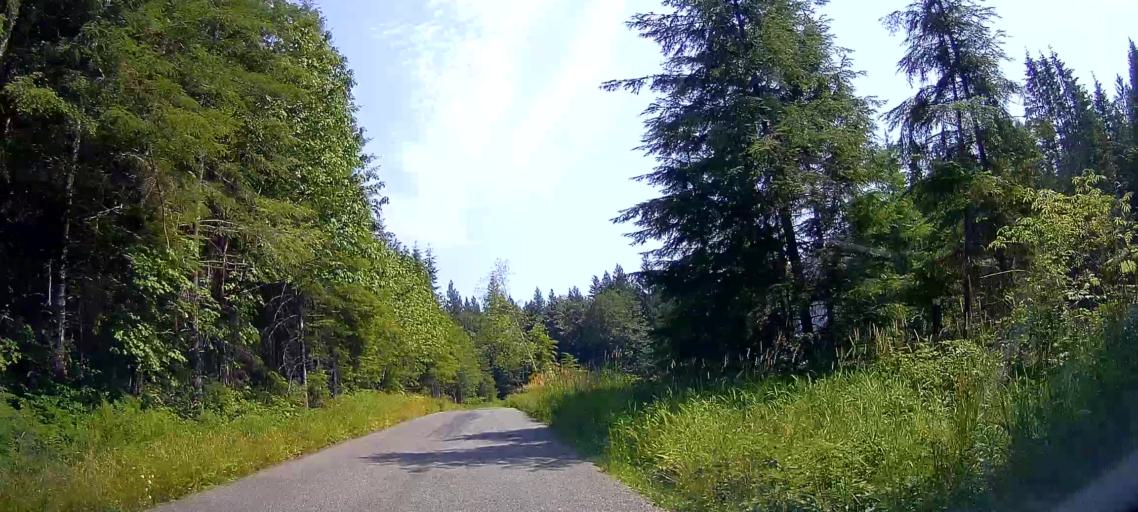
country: US
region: Washington
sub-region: Snohomish County
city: Arlington Heights
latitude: 48.3337
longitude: -122.0168
